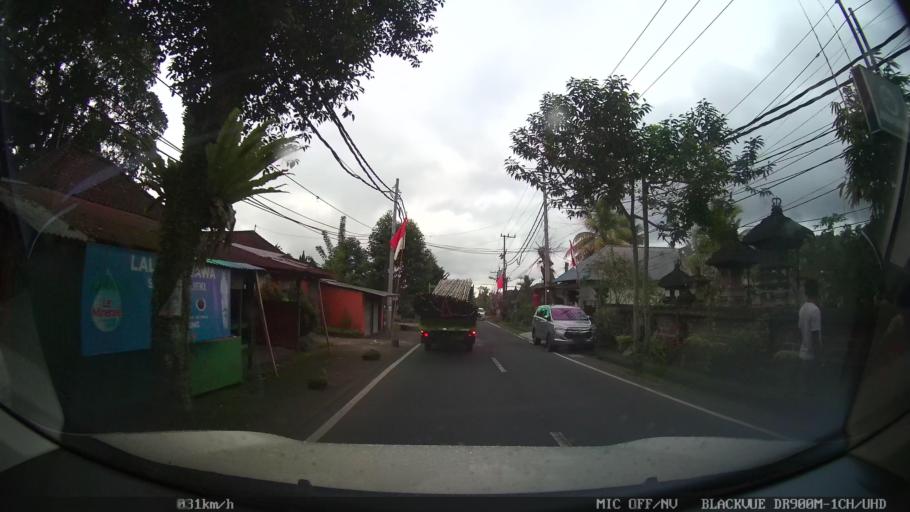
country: ID
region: Bali
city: Badung
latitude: -8.4375
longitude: 115.2446
